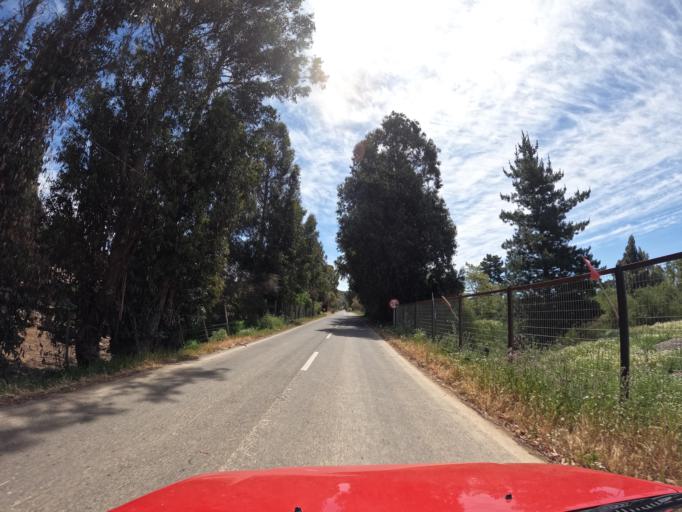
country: CL
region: Maule
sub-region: Provincia de Talca
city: Talca
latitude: -35.0566
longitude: -71.7432
